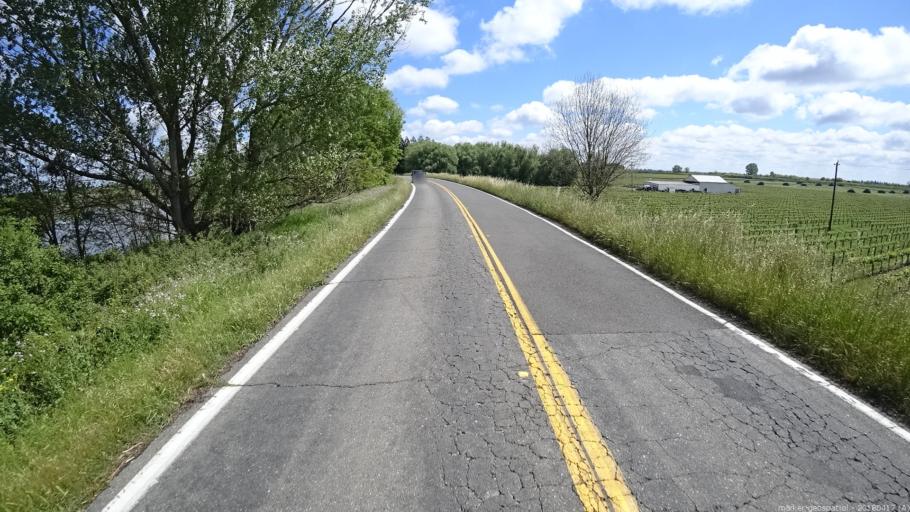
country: US
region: California
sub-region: Sacramento County
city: Walnut Grove
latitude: 38.1928
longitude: -121.5644
